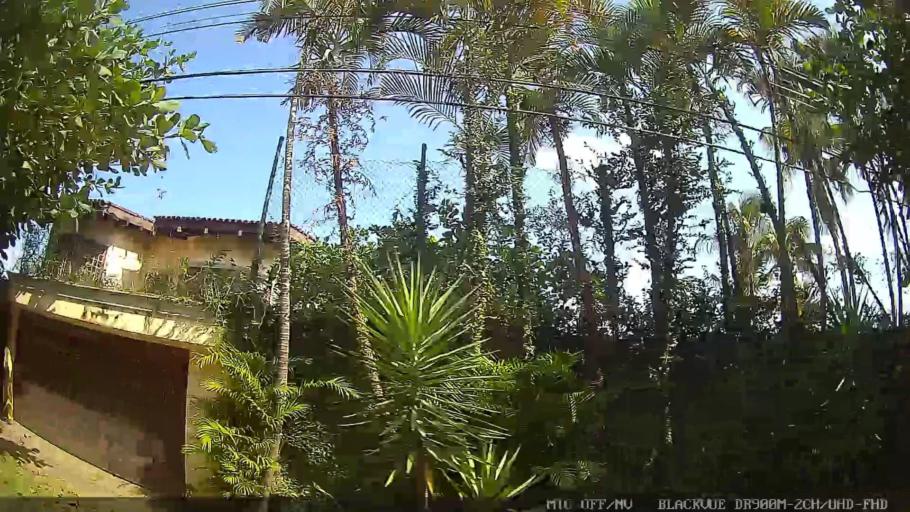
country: BR
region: Sao Paulo
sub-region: Guaruja
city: Guaruja
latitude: -23.9809
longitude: -46.2090
